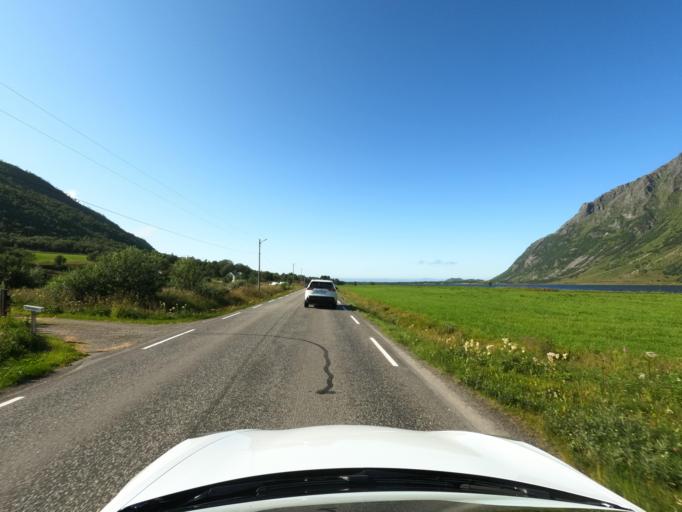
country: NO
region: Nordland
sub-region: Vestvagoy
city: Evjen
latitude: 68.2765
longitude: 13.9239
